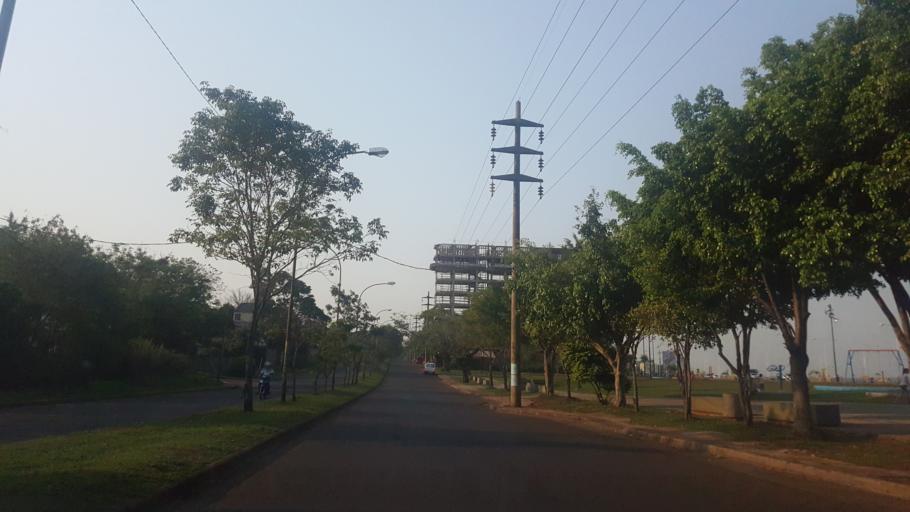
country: AR
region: Misiones
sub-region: Departamento de Capital
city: Posadas
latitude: -27.3950
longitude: -55.8938
